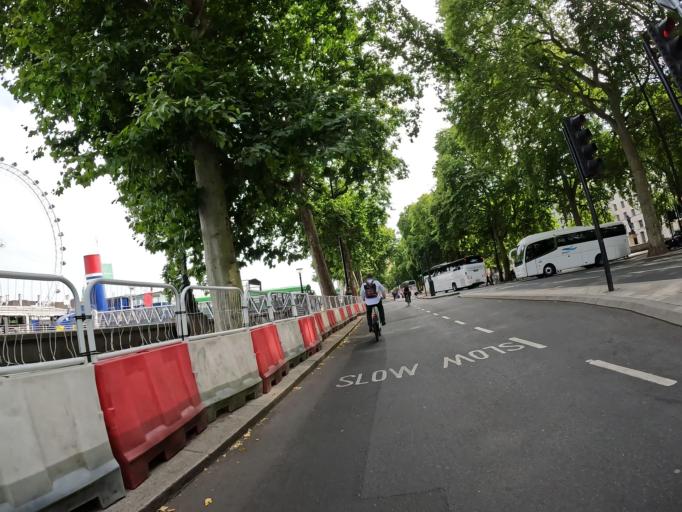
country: GB
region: England
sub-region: Greater London
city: Blackheath
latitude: 51.4402
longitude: 0.0059
